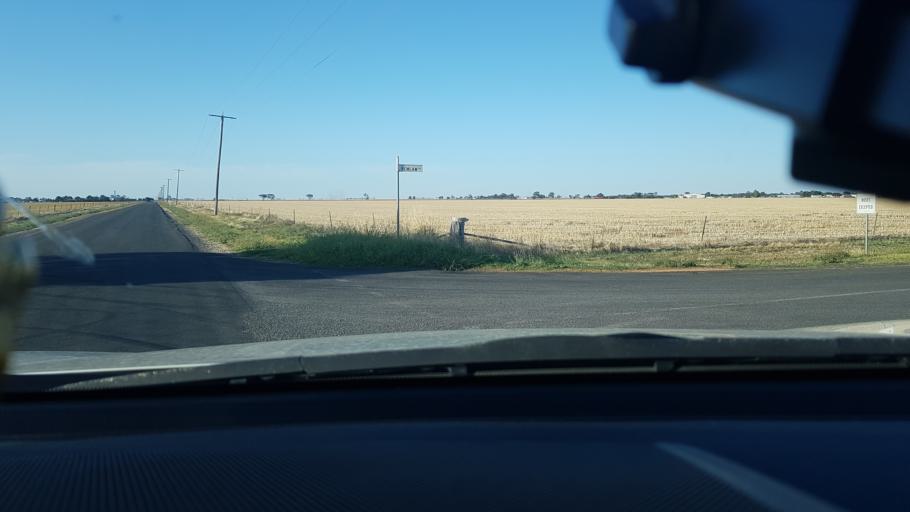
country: AU
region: Victoria
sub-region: Horsham
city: Horsham
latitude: -36.7135
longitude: 142.1689
